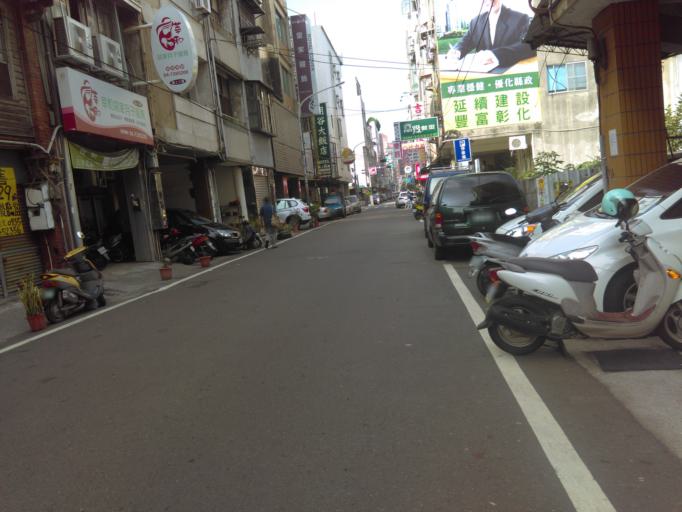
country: TW
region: Taiwan
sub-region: Changhua
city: Chang-hua
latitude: 24.0798
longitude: 120.5415
